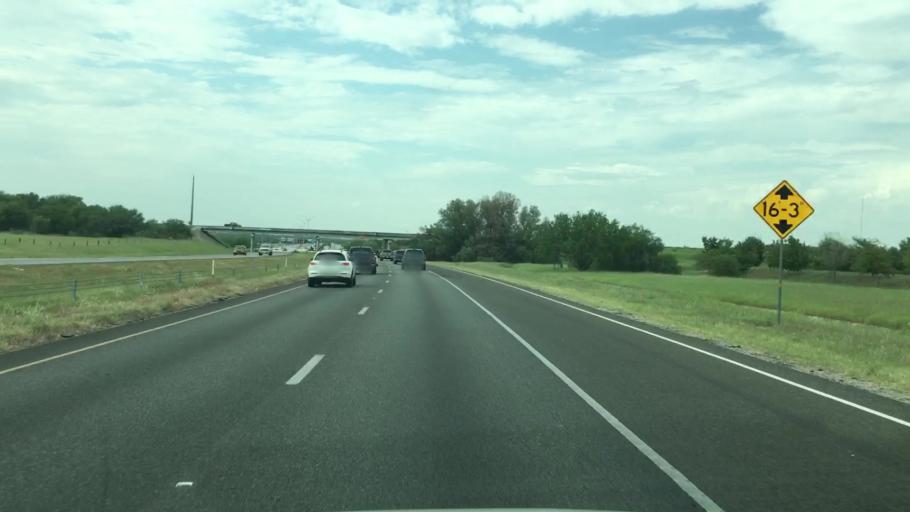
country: US
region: Texas
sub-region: Bexar County
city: Elmendorf
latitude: 29.3057
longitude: -98.3977
